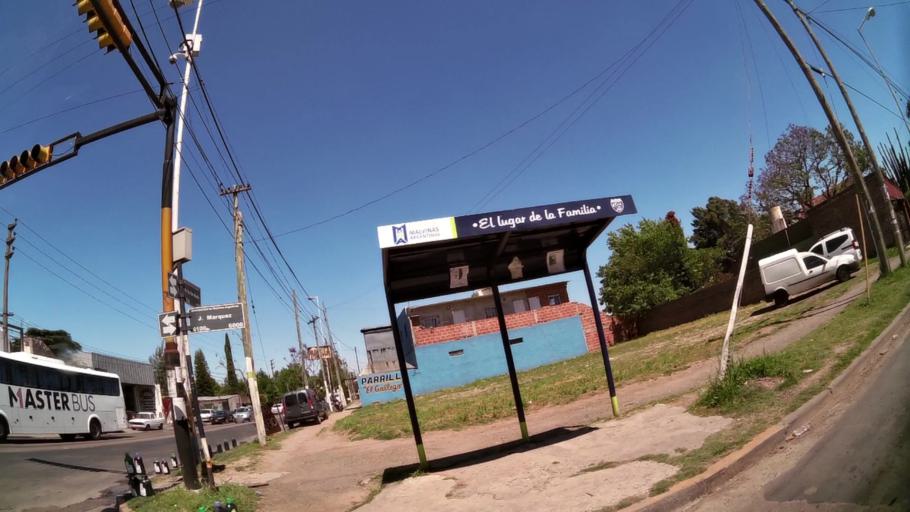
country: AR
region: Buenos Aires
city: Hurlingham
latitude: -34.4936
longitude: -58.6559
